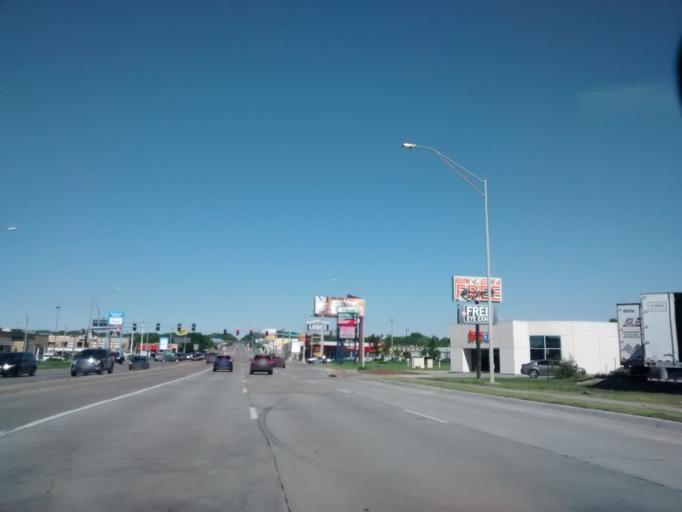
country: US
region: Nebraska
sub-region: Douglas County
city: Ralston
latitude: 41.2596
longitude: -96.0332
